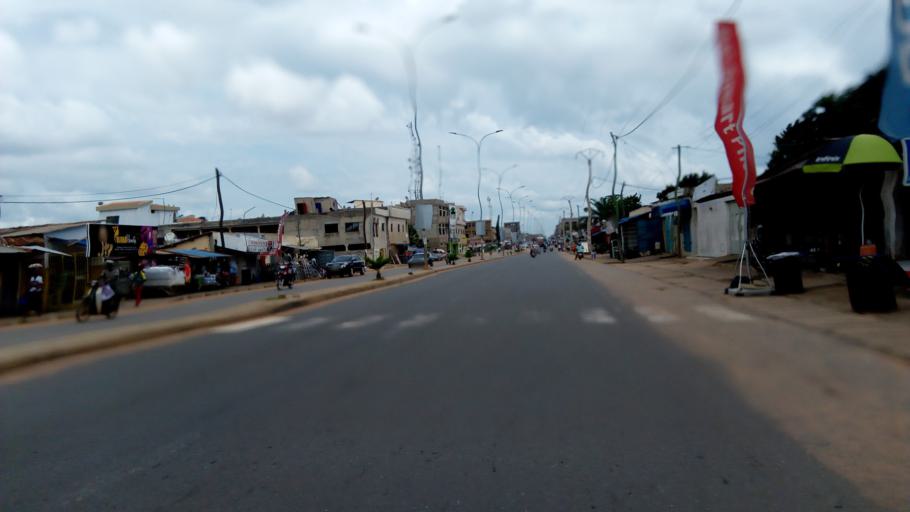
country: TG
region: Maritime
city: Lome
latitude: 6.2106
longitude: 1.1783
